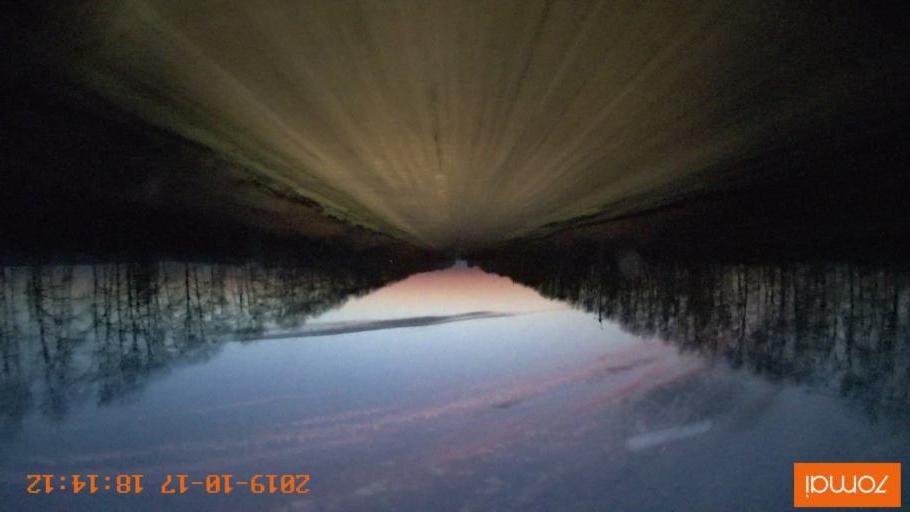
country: RU
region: Tula
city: Kurkino
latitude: 53.4079
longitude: 38.5682
